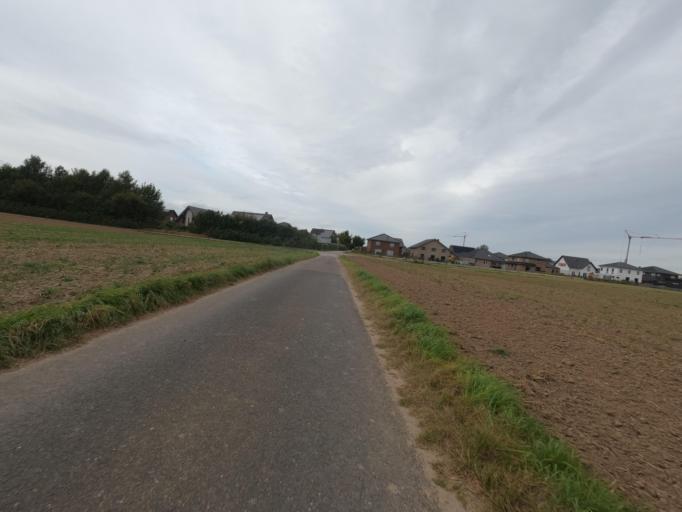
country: DE
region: North Rhine-Westphalia
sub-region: Regierungsbezirk Koln
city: Linnich
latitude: 50.9921
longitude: 6.2124
